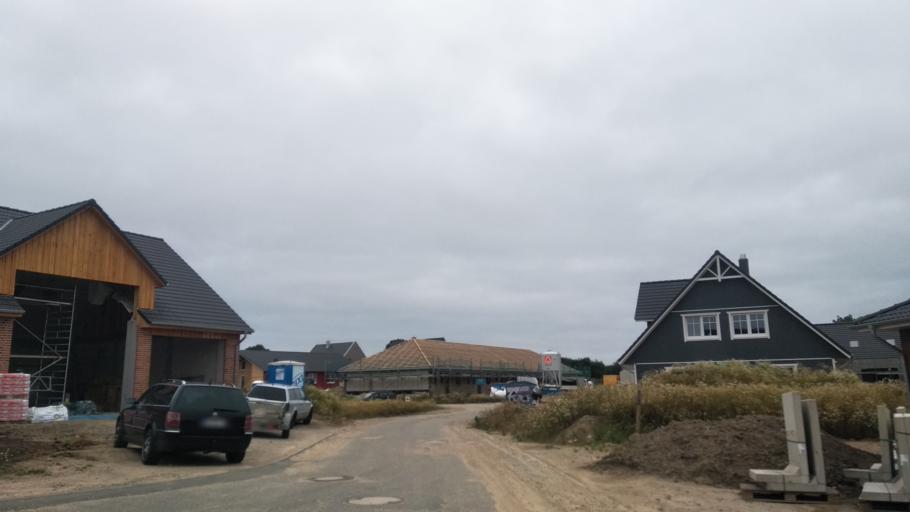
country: DE
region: Schleswig-Holstein
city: Langballig
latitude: 54.7993
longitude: 9.6294
